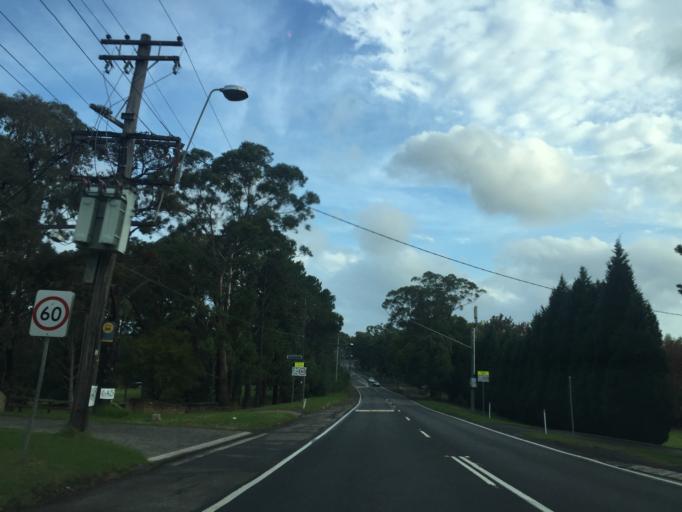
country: AU
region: New South Wales
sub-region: The Hills Shire
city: Glenhaven
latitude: -33.6998
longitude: 151.0156
